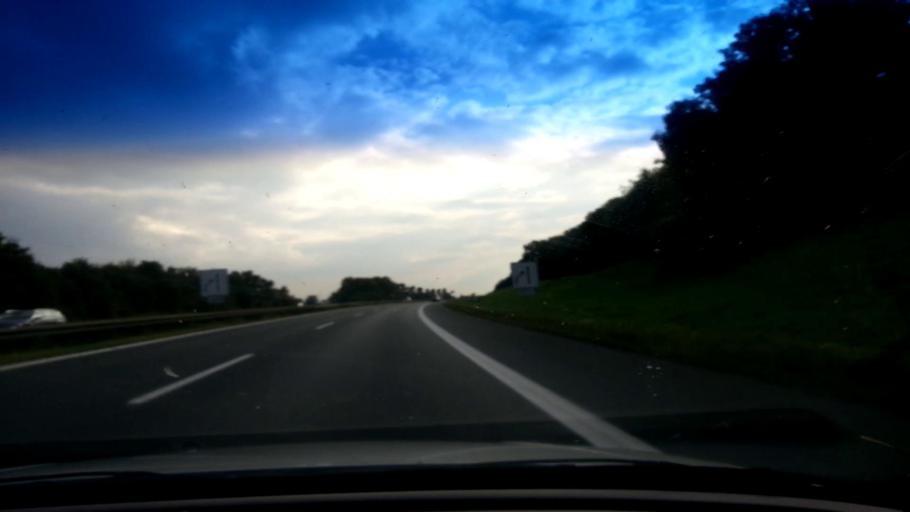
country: DE
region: Bavaria
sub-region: Upper Franconia
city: Memmelsdorf
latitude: 49.9572
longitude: 10.9836
